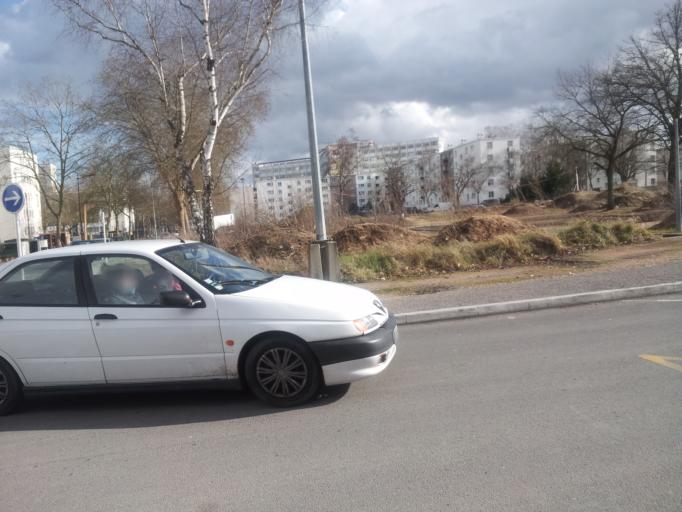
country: FR
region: Centre
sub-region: Departement du Loiret
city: Saint-Cyr-en-Val
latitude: 47.8376
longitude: 1.9288
